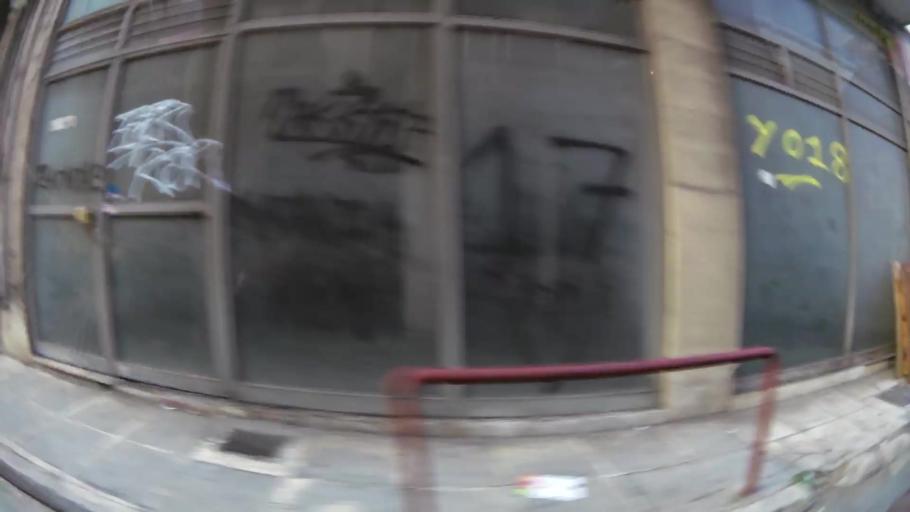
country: GR
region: Attica
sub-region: Nomarchia Athinas
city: Dhafni
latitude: 37.9574
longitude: 23.7383
